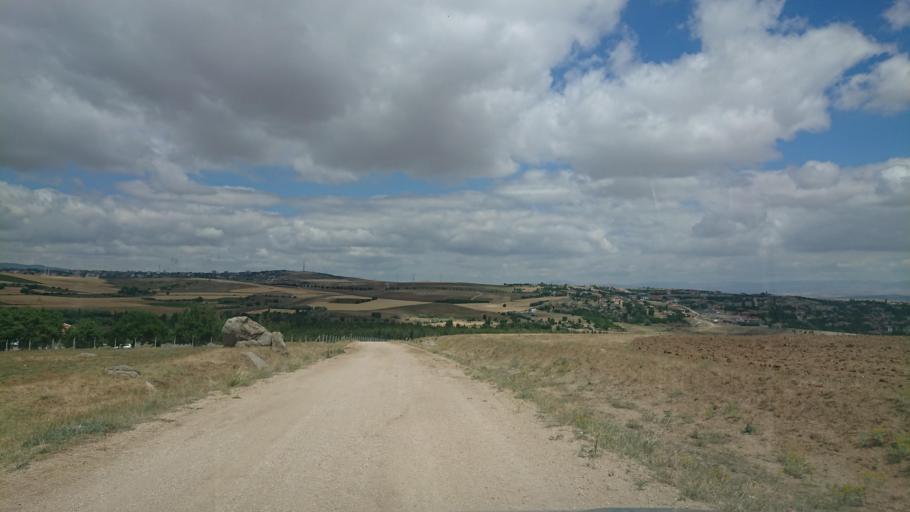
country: TR
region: Aksaray
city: Agacoren
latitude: 38.8571
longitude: 33.9494
